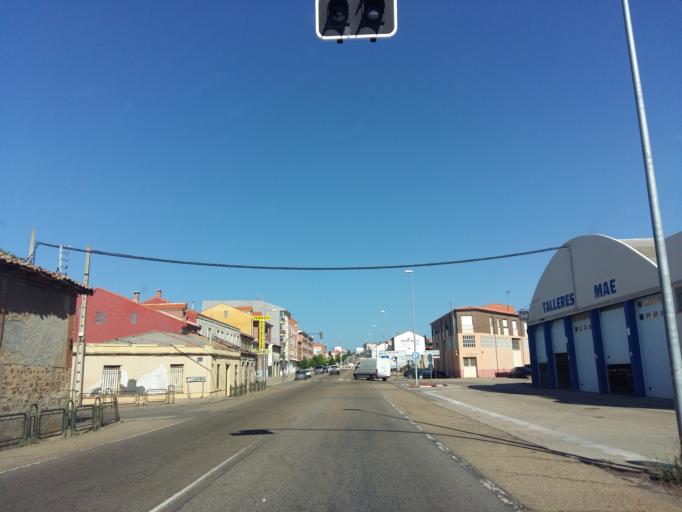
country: ES
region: Castille and Leon
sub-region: Provincia de Leon
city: Astorga
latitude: 42.4505
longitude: -6.0528
